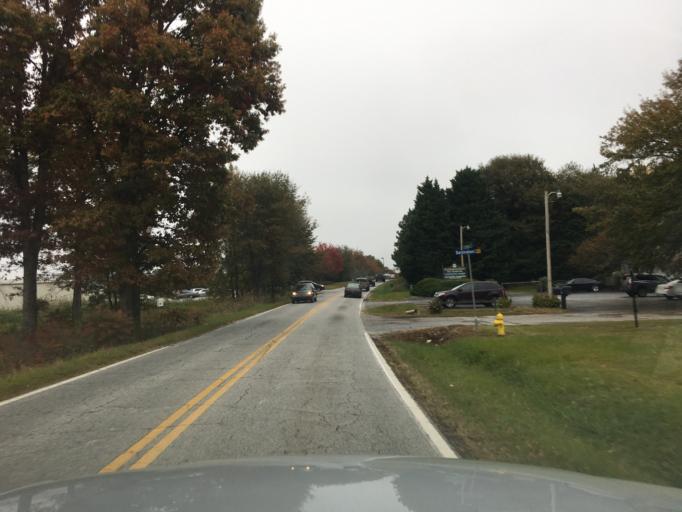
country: US
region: South Carolina
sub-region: Greenville County
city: Five Forks
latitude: 34.8165
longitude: -82.2722
